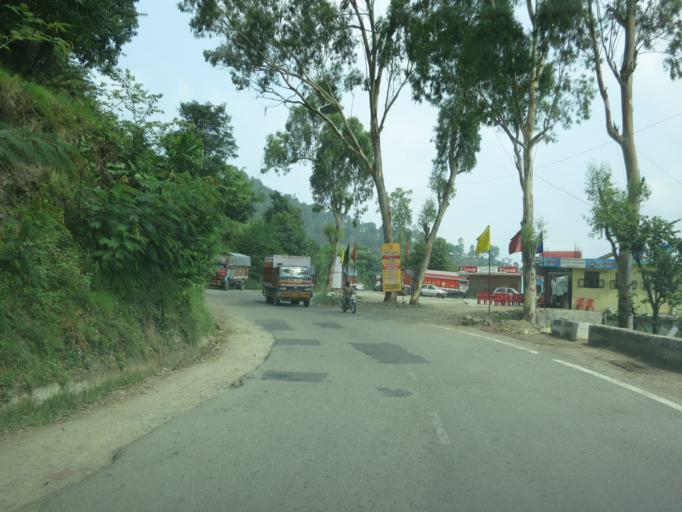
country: IN
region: Himachal Pradesh
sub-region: Solan
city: Arki
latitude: 31.2558
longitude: 76.8740
